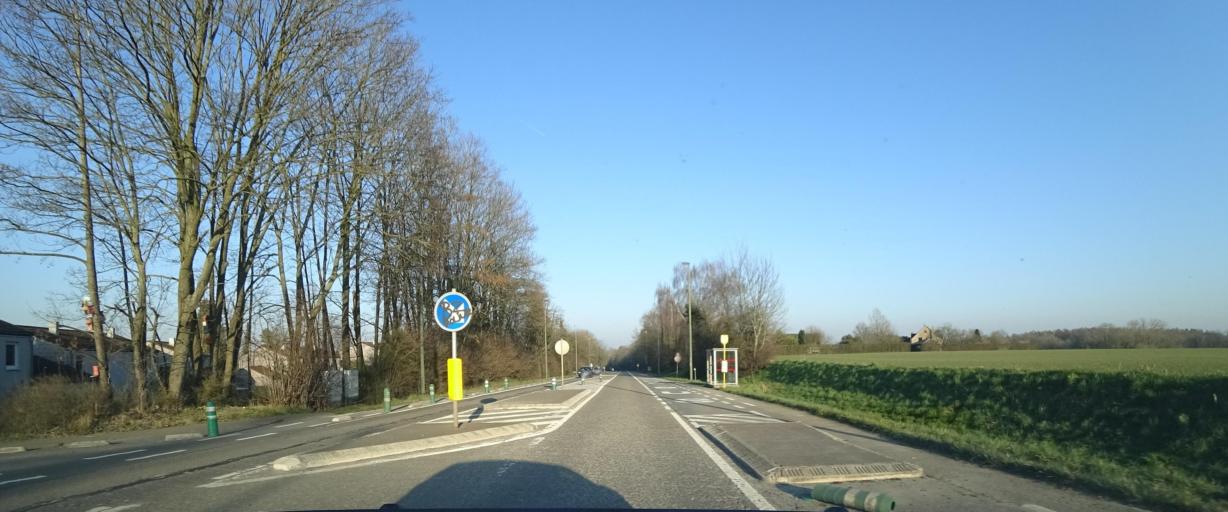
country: BE
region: Wallonia
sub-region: Province du Brabant Wallon
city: Ottignies
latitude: 50.6503
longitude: 4.5458
